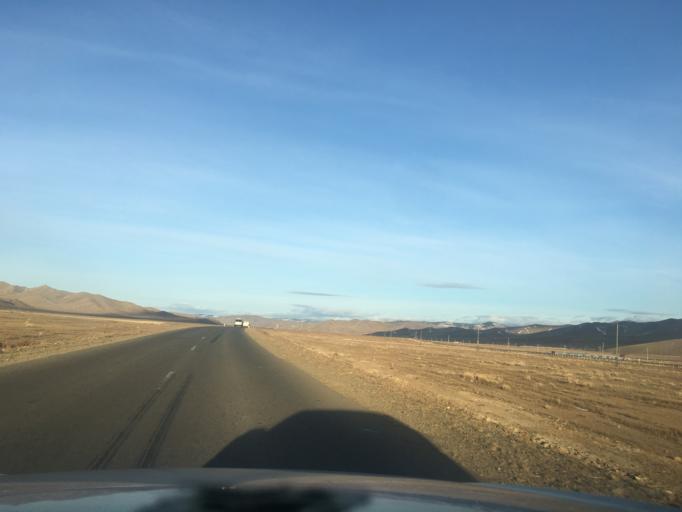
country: MN
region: Central Aimak
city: Mandal
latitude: 48.0832
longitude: 106.5881
